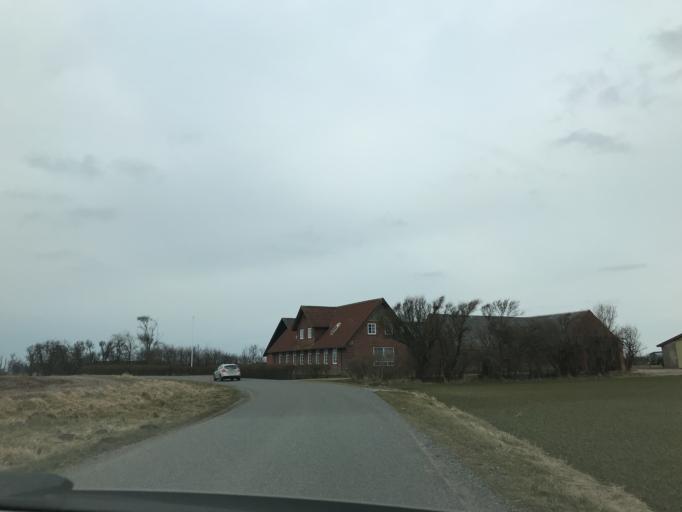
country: DK
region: South Denmark
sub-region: Varde Kommune
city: Oksbol
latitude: 55.8165
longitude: 8.2905
